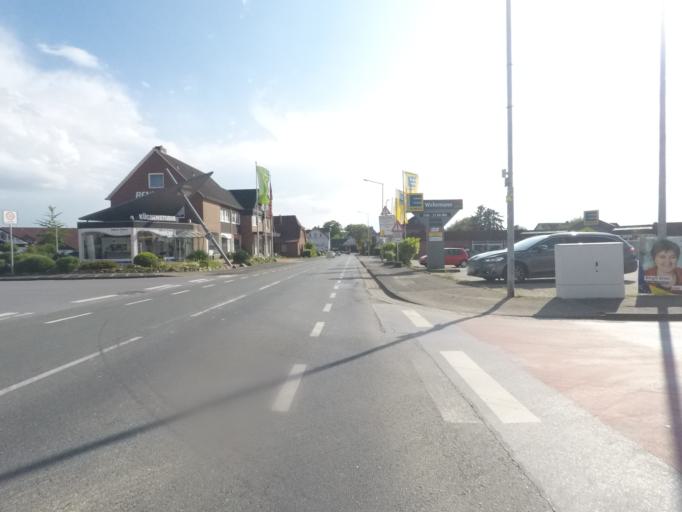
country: DE
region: North Rhine-Westphalia
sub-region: Regierungsbezirk Detmold
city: Hiddenhausen
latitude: 52.1677
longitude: 8.6337
